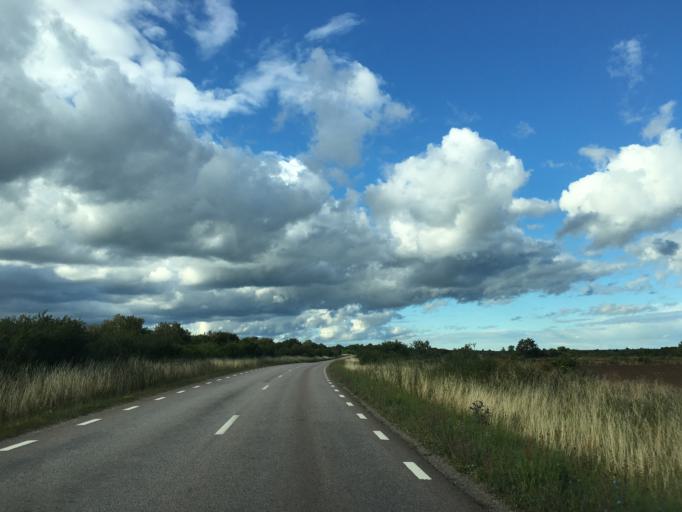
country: SE
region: Kalmar
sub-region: Morbylanga Kommun
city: Moerbylanga
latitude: 56.5497
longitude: 16.4427
